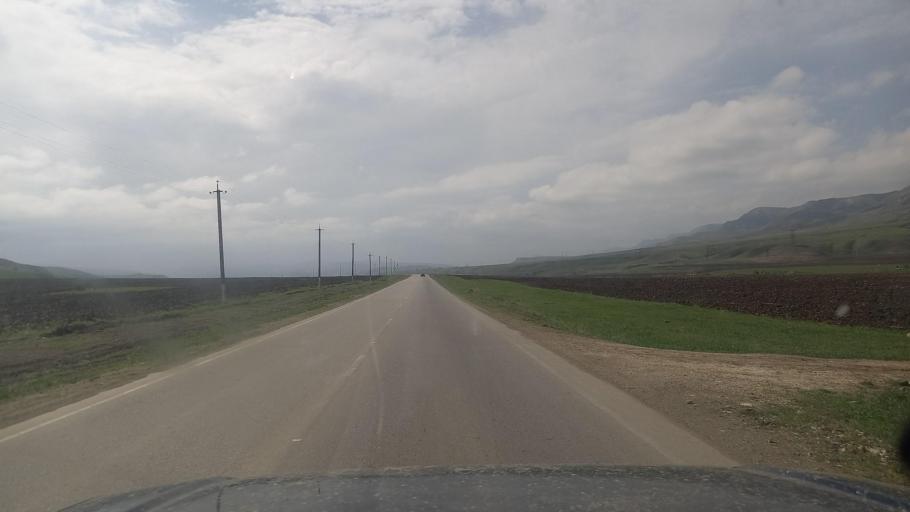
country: RU
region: Kabardino-Balkariya
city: Kamennomostskoye
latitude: 43.7275
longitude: 43.1099
